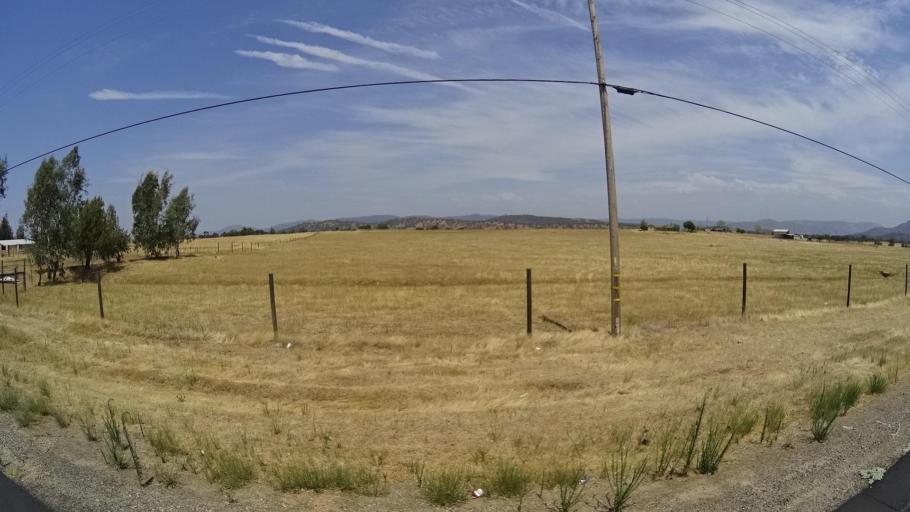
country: US
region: California
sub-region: Tuolumne County
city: Jamestown
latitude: 37.6461
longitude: -120.3225
